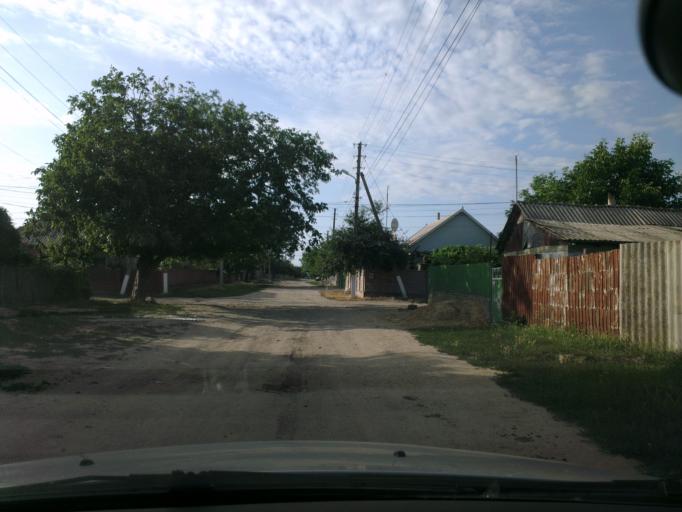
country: MD
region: Cahul
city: Cahul
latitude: 45.9187
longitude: 28.2038
